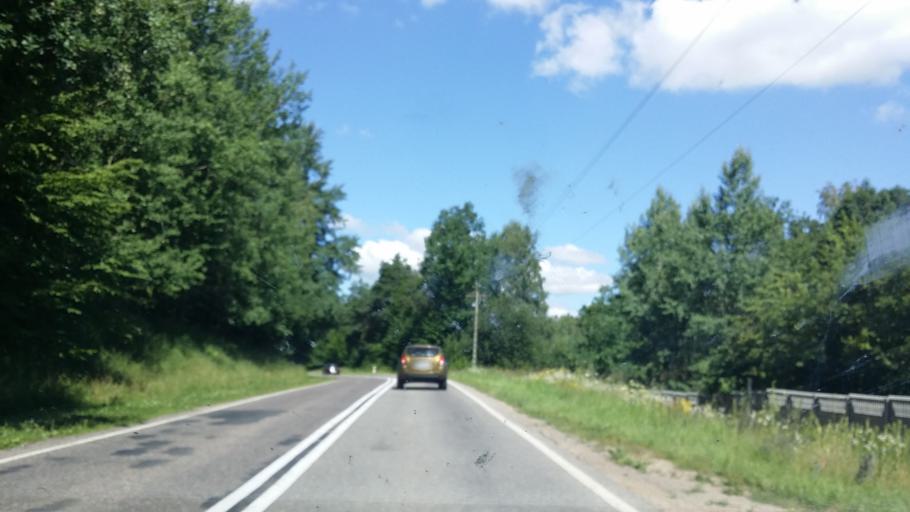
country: PL
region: West Pomeranian Voivodeship
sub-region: Powiat drawski
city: Drawsko Pomorskie
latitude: 53.5080
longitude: 15.7933
